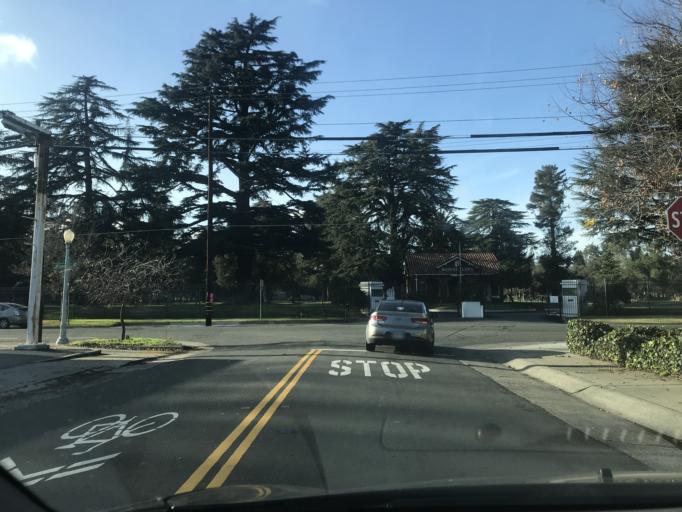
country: US
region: California
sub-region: Sacramento County
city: Sacramento
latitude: 38.5595
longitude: -121.5001
